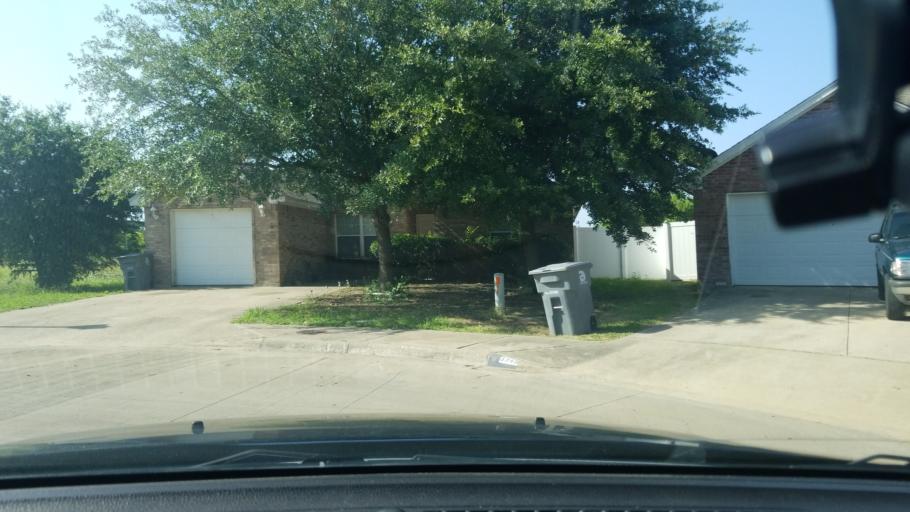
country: US
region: Texas
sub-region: Dallas County
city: Mesquite
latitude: 32.8042
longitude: -96.6746
